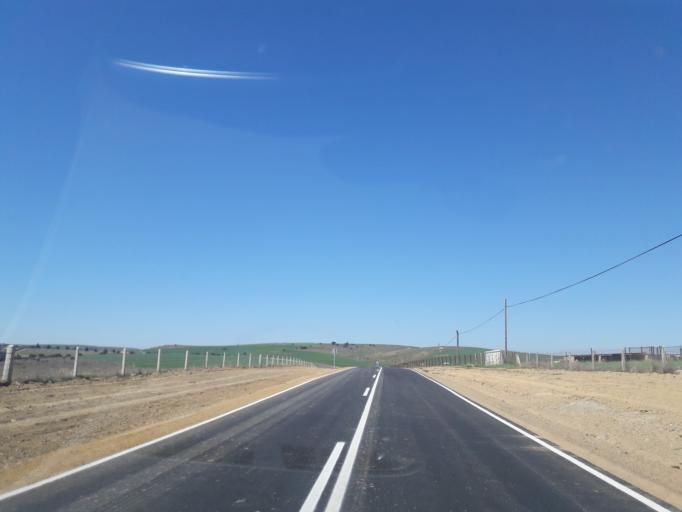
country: ES
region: Castille and Leon
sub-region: Provincia de Salamanca
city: Terradillos
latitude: 40.8254
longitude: -5.5425
